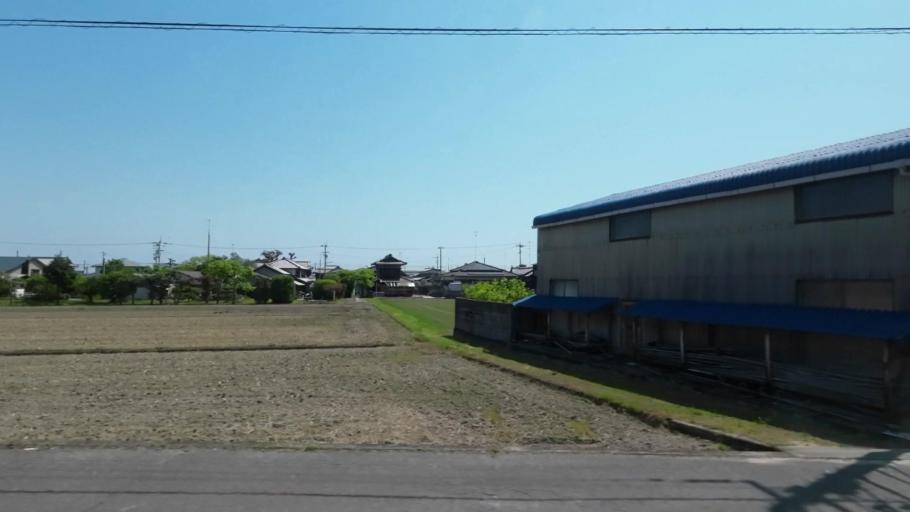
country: JP
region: Ehime
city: Saijo
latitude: 34.0138
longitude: 133.0352
